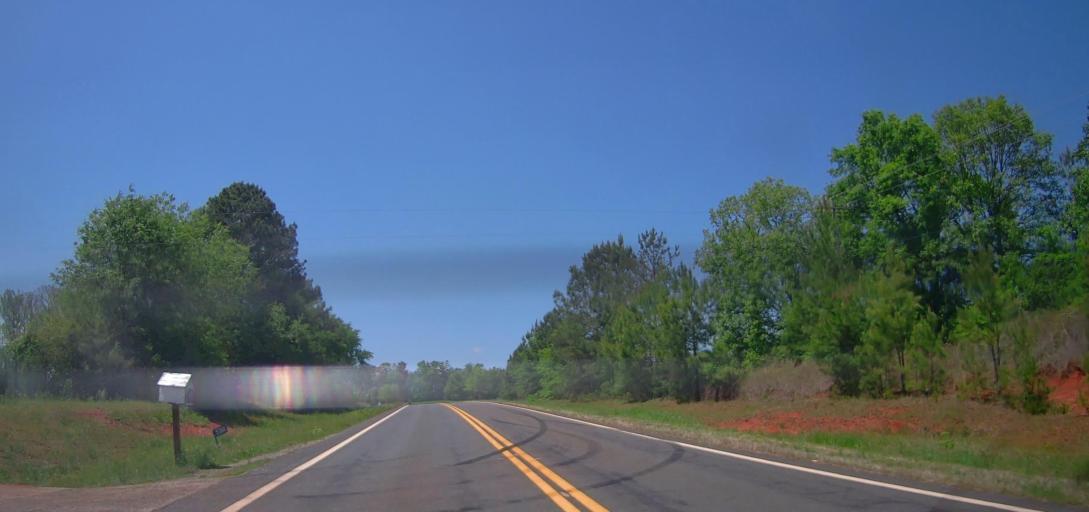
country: US
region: Georgia
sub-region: Jasper County
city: Monticello
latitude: 33.2713
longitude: -83.5899
